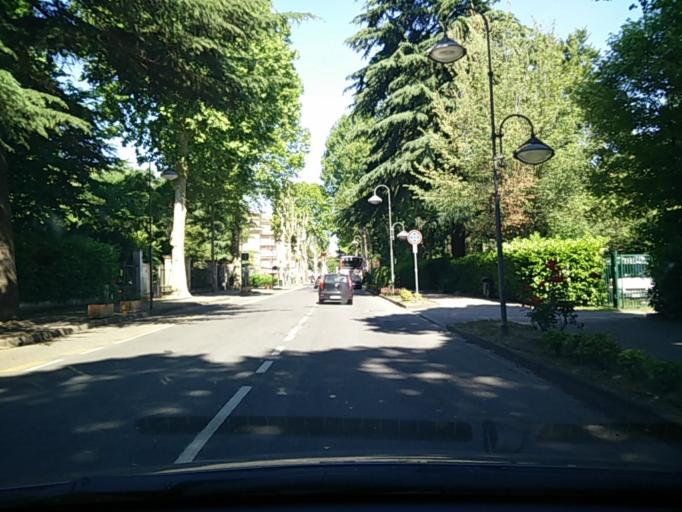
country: IT
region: Lombardy
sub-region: Provincia di Pavia
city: Salice Terme
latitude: 44.9142
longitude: 9.0282
